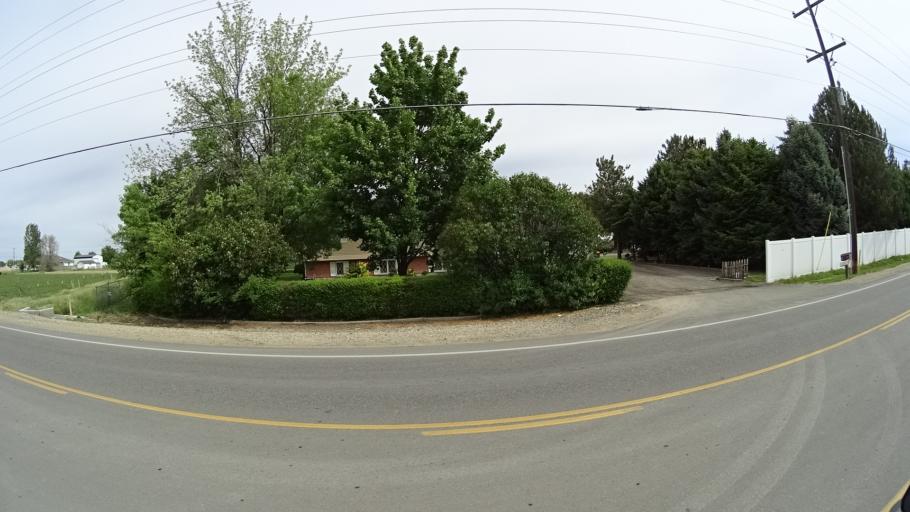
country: US
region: Idaho
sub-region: Ada County
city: Meridian
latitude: 43.5465
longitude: -116.3117
